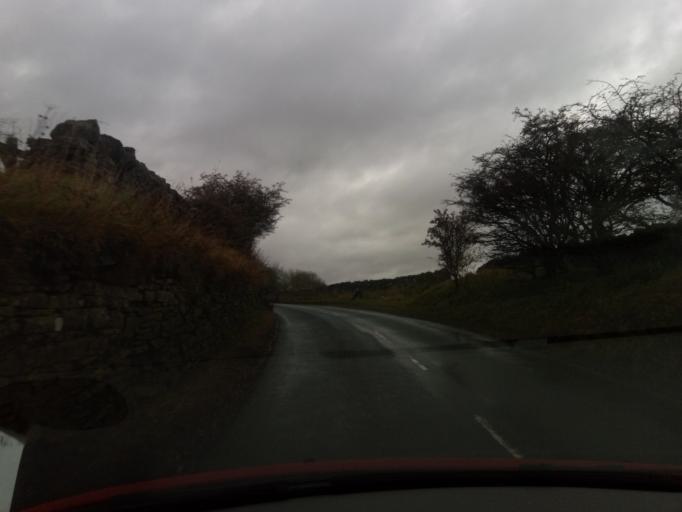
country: GB
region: England
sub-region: County Durham
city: Muggleswick
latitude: 54.8486
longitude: -1.9667
